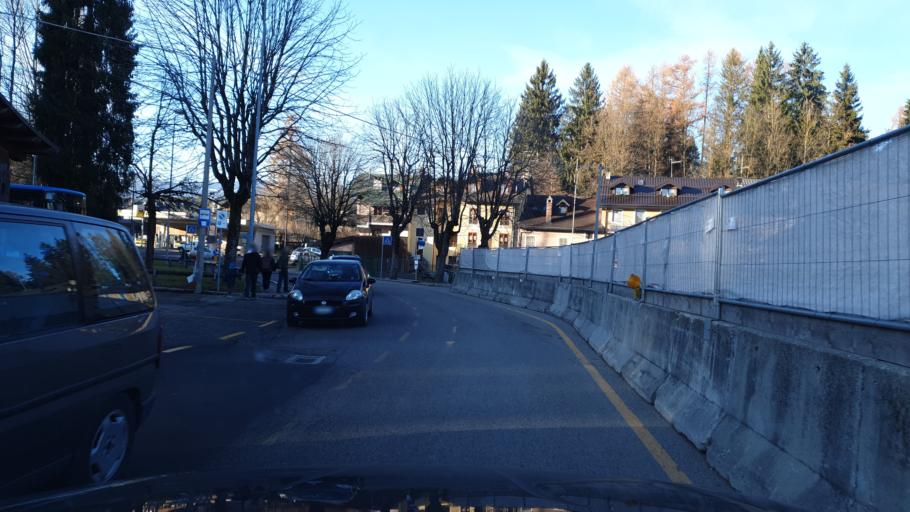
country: IT
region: Veneto
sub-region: Provincia di Vicenza
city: Asiago
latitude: 45.8730
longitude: 11.5066
